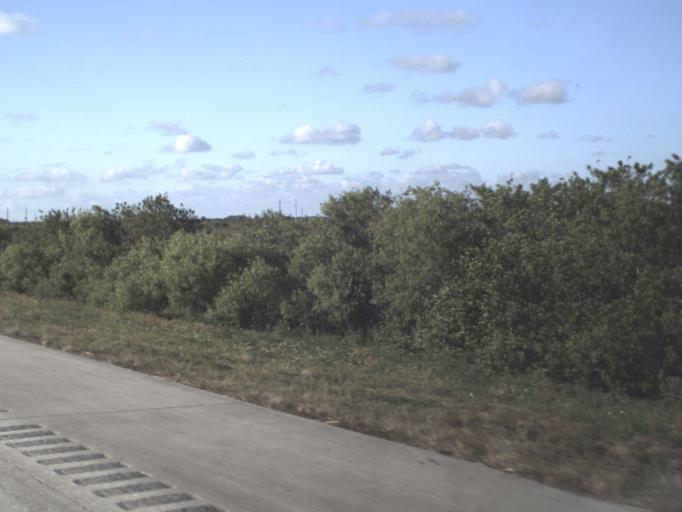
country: US
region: Florida
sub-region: Brevard County
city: Cocoa West
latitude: 28.3128
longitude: -80.7635
